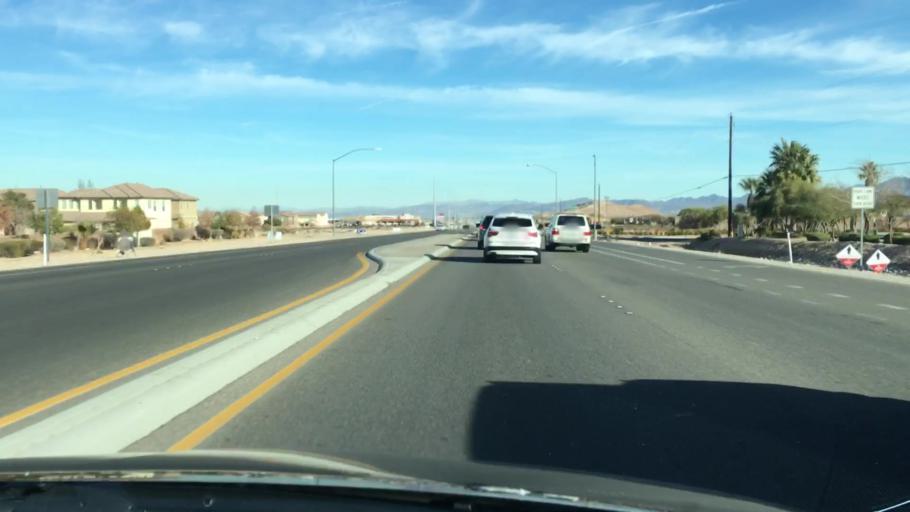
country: US
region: Nevada
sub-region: Clark County
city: Enterprise
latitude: 36.0201
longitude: -115.2864
